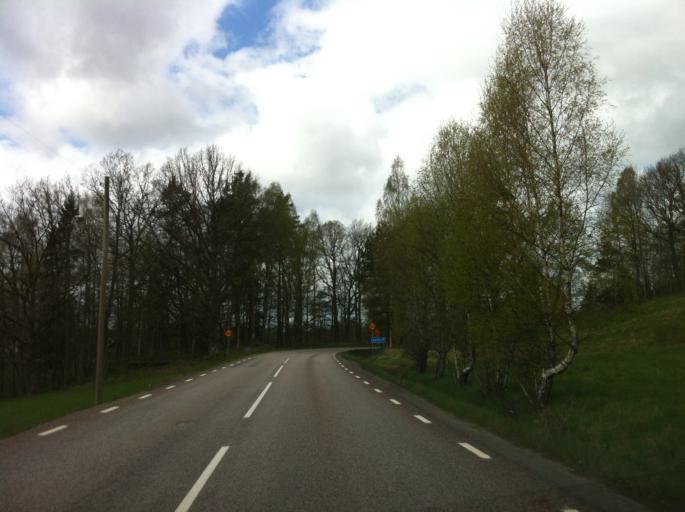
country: SE
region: Vaestra Goetaland
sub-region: Alingsas Kommun
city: Ingared
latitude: 57.8429
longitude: 12.4913
